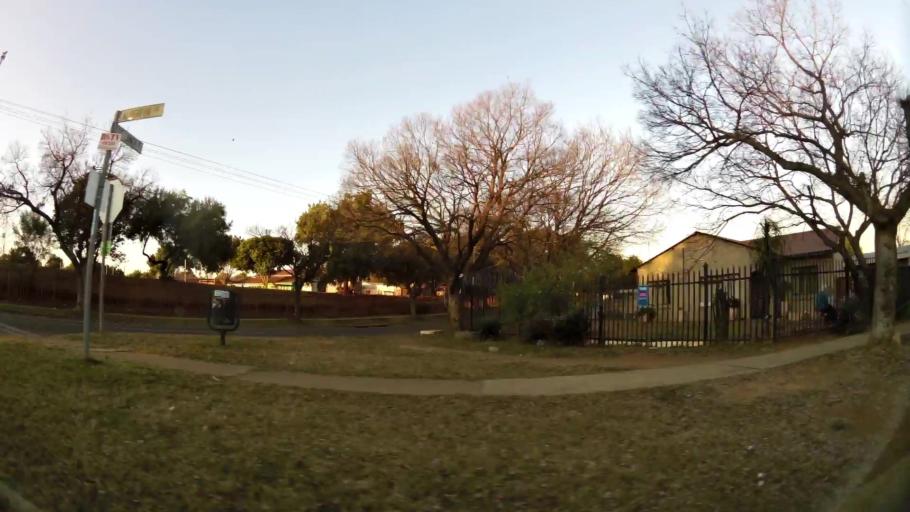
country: ZA
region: Gauteng
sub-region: City of Tshwane Metropolitan Municipality
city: Pretoria
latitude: -25.7435
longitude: 28.1255
